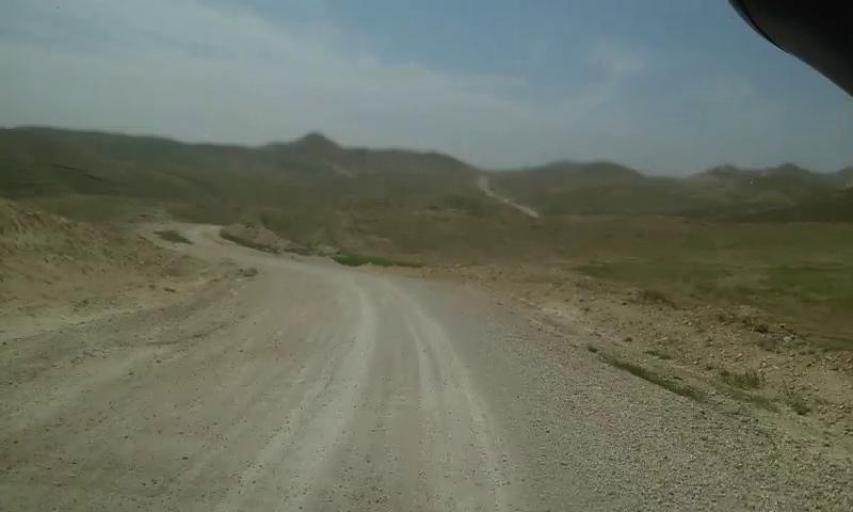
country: PS
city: `Arab ar Rashaydah
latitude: 31.4919
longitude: 35.2896
